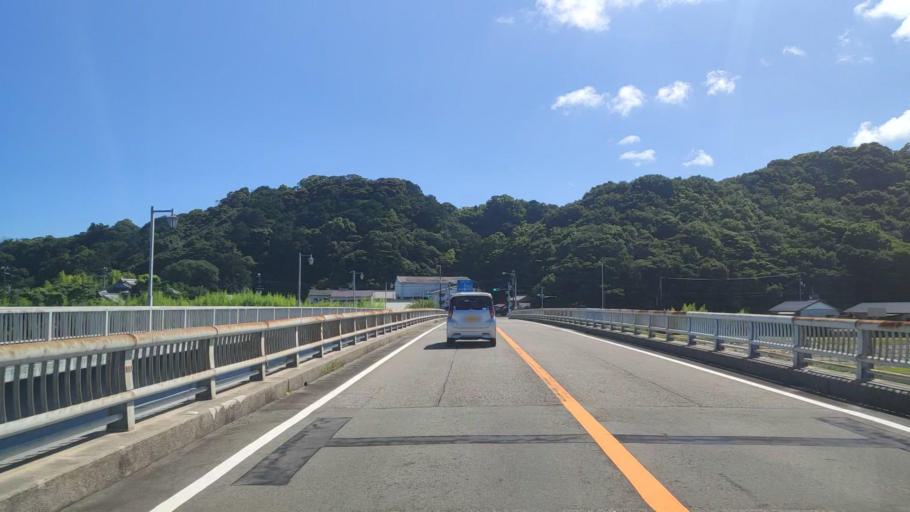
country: JP
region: Wakayama
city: Shingu
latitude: 33.5791
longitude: 135.9193
